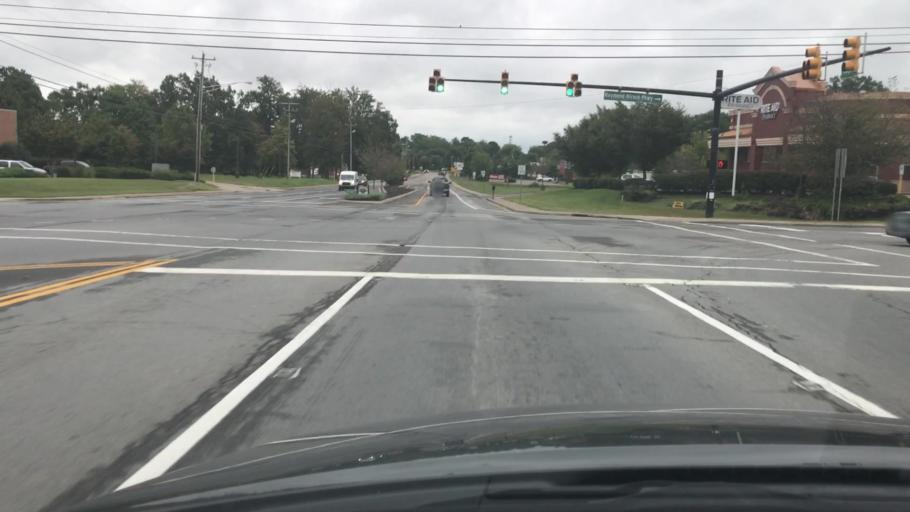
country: US
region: Tennessee
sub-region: Sumner County
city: White House
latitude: 36.4686
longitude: -86.6657
